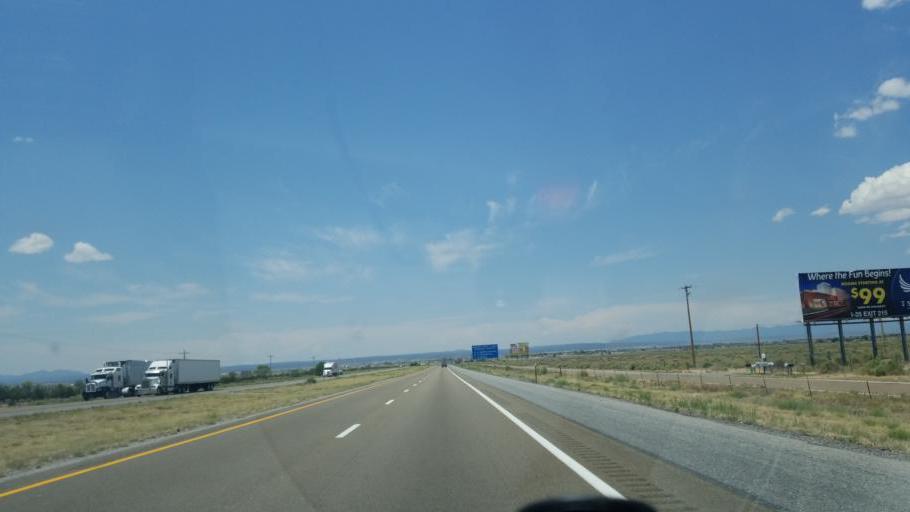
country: US
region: New Mexico
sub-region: Torrance County
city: Moriarty
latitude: 35.0049
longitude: -105.9784
